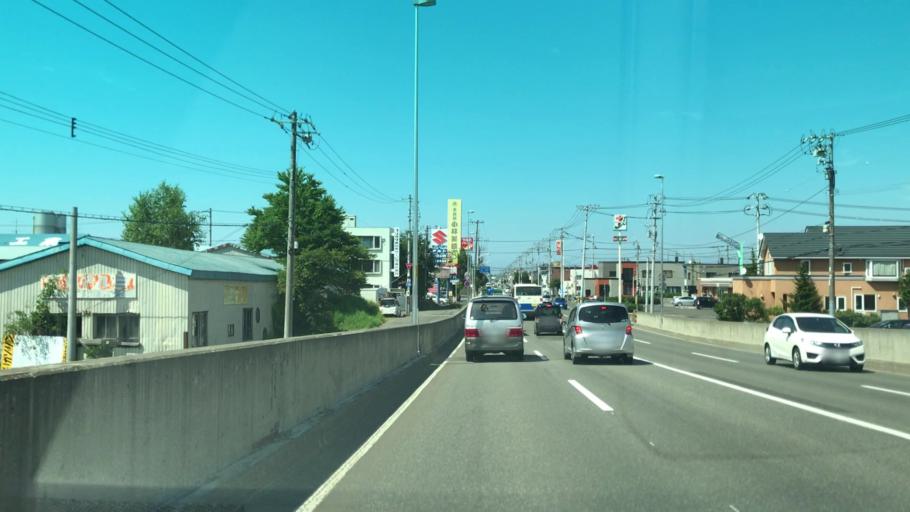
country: JP
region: Hokkaido
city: Sapporo
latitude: 43.1267
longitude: 141.2358
